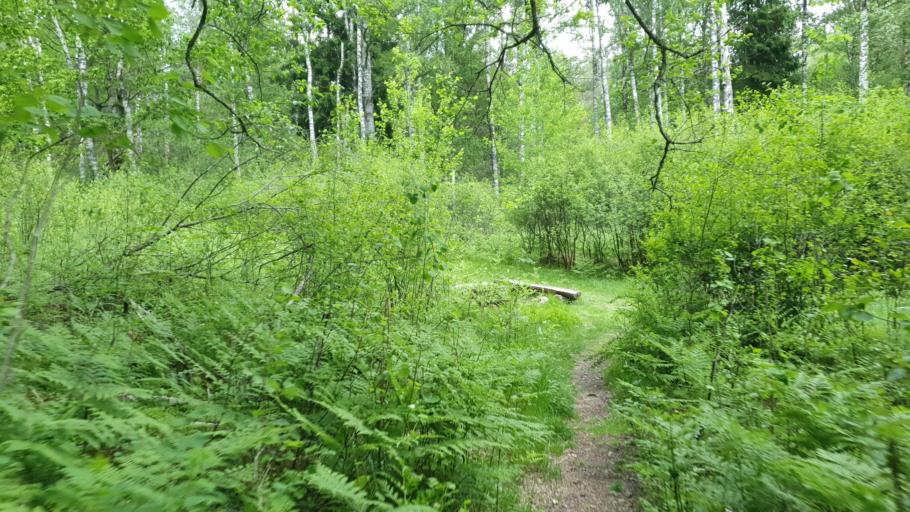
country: SE
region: Vaestra Goetaland
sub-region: Molndal
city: Kallered
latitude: 57.6154
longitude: 12.0526
